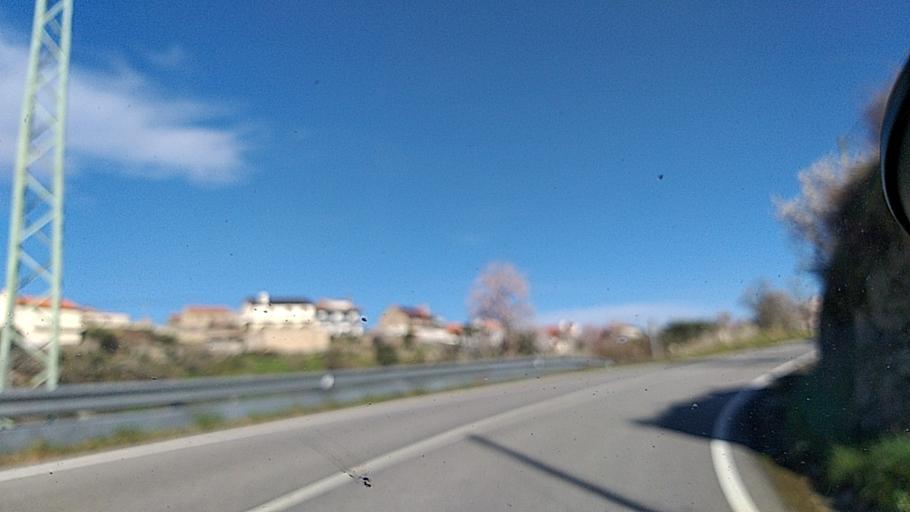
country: ES
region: Castille and Leon
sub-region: Provincia de Salamanca
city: Fuentes de Onoro
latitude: 40.6190
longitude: -6.9014
